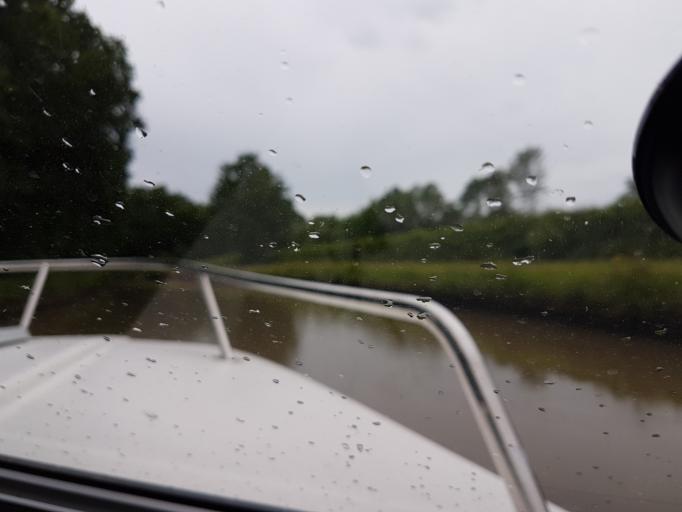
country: FR
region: Bourgogne
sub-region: Departement de la Nievre
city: Clamecy
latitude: 47.3667
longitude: 3.6116
